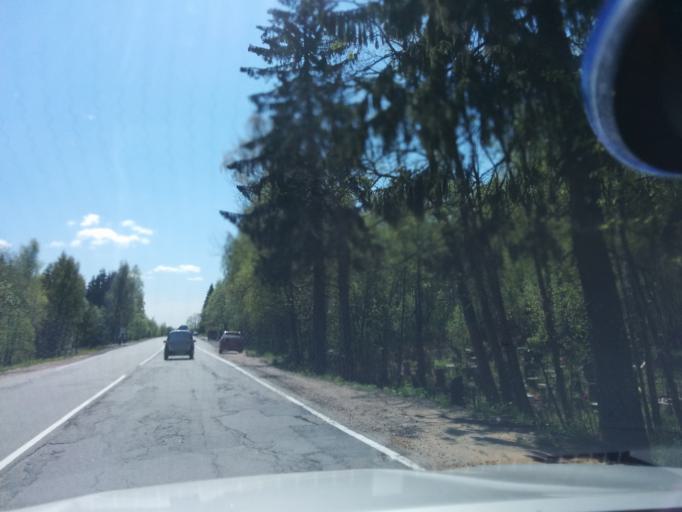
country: RU
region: Leningrad
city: Verkhniye Osel'ki
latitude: 60.2291
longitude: 30.4323
